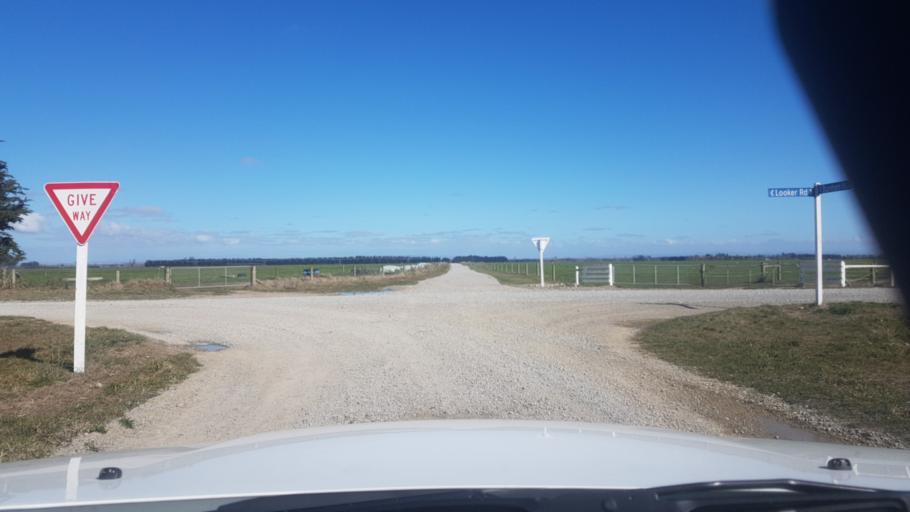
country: NZ
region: Canterbury
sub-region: Timaru District
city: Pleasant Point
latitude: -44.1370
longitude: 171.3808
